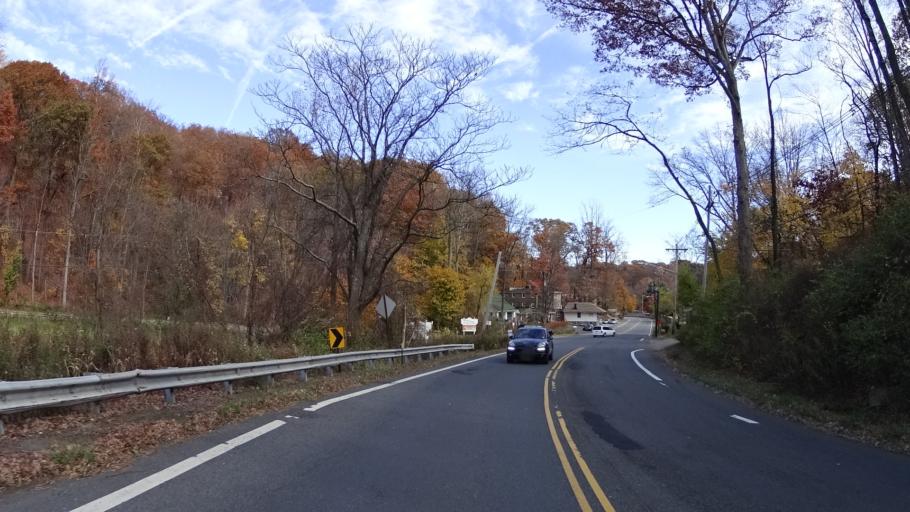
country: US
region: New Jersey
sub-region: Morris County
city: Morristown
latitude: 40.7997
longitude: -74.5022
